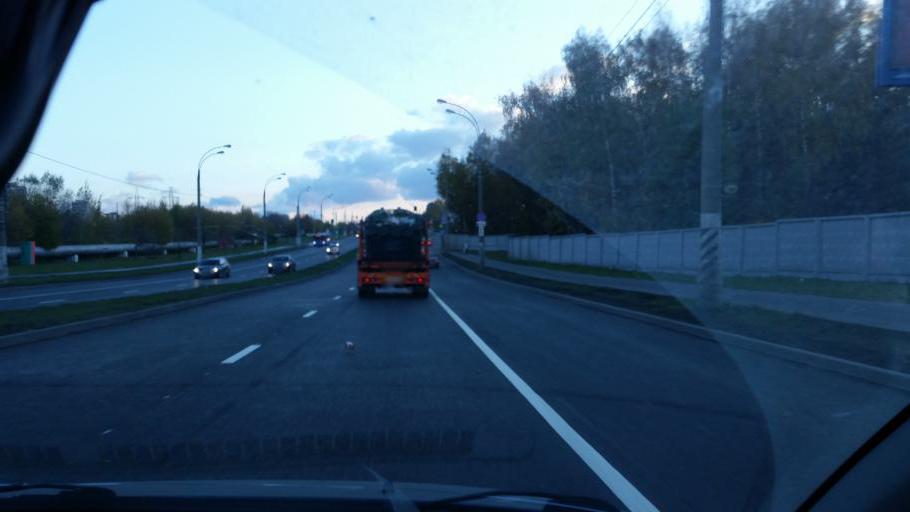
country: RU
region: Moskovskaya
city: Biryulevo Zapadnoye
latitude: 55.5956
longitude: 37.6359
